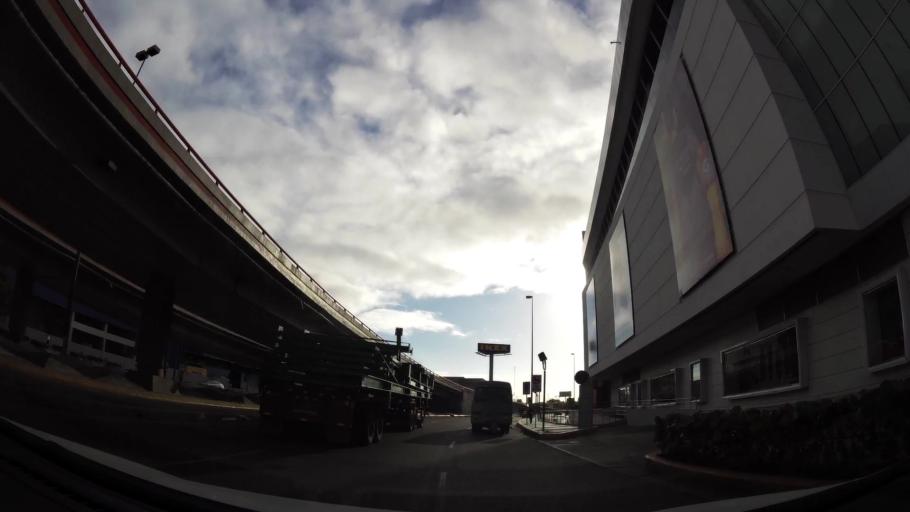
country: DO
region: Nacional
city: La Agustina
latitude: 18.4842
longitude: -69.9400
